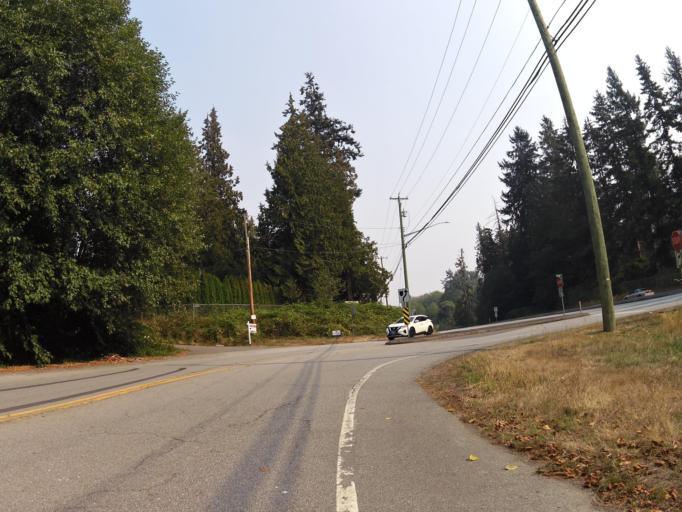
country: US
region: Washington
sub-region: Whatcom County
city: Blaine
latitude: 49.0168
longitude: -122.7549
